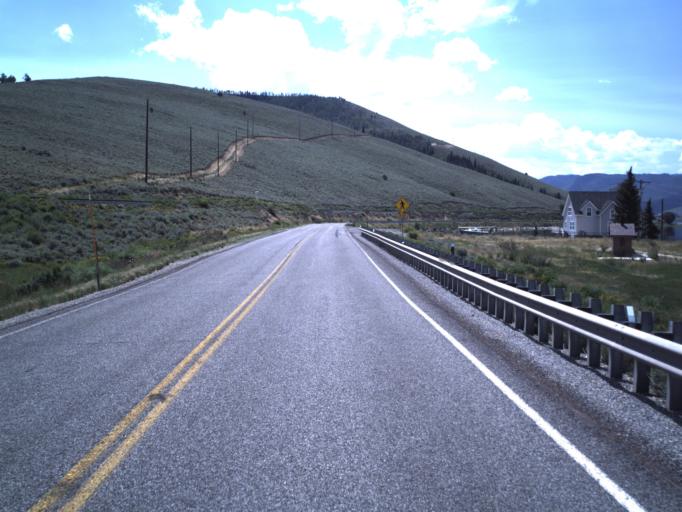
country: US
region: Utah
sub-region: Carbon County
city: Helper
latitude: 39.7854
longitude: -111.1336
